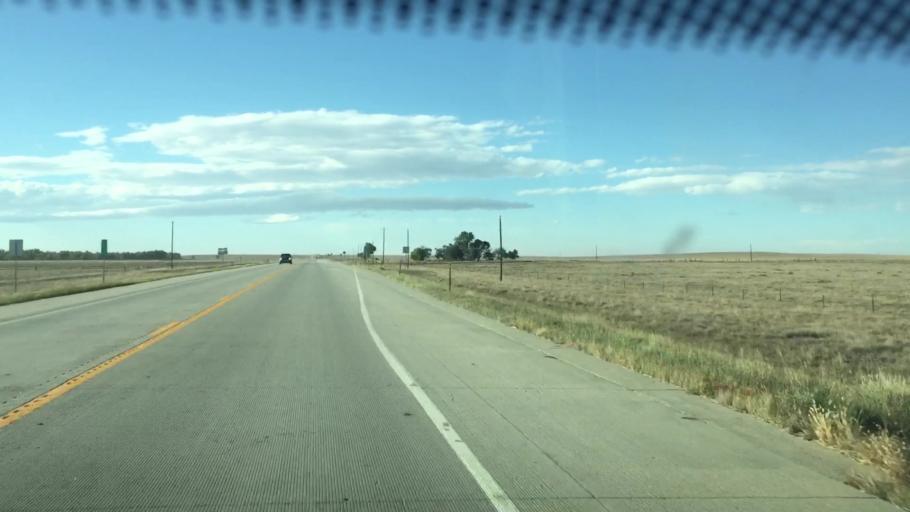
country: US
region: Colorado
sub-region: Lincoln County
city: Hugo
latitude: 39.0490
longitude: -103.3473
